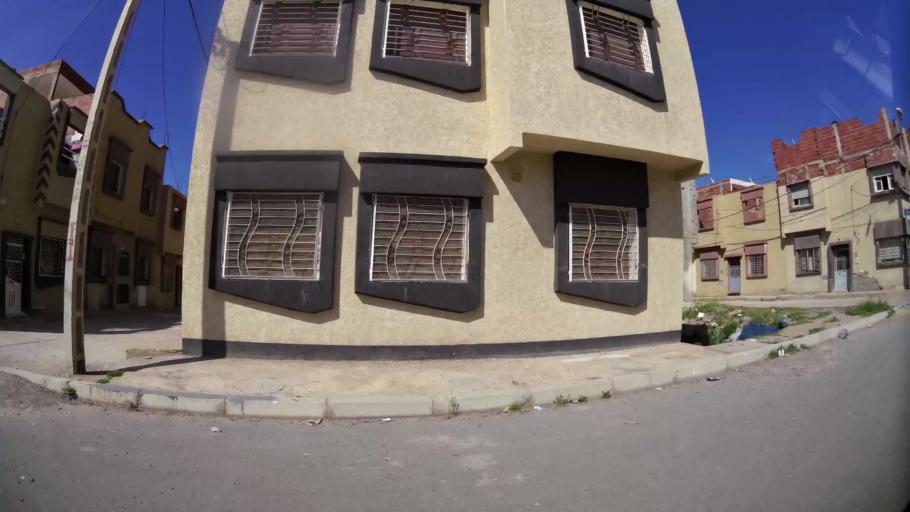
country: MA
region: Oriental
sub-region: Oujda-Angad
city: Oujda
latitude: 34.6963
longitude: -1.8762
